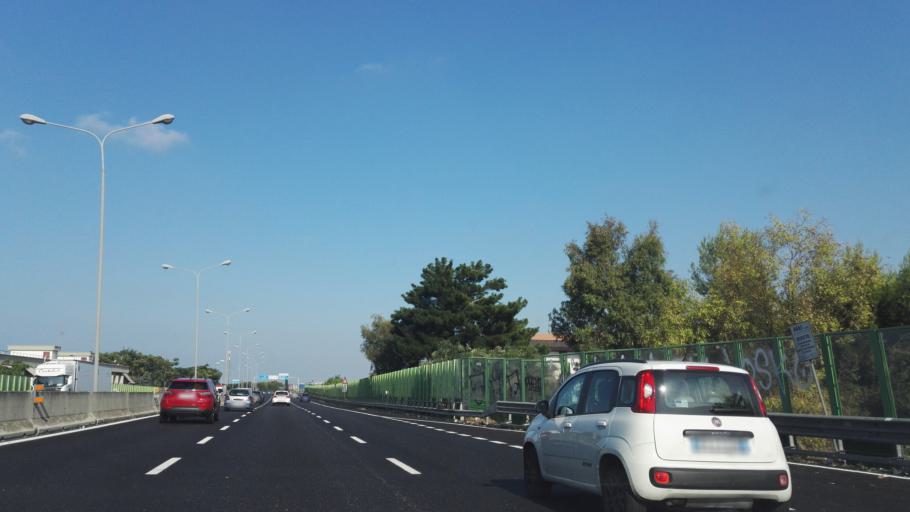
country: IT
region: Apulia
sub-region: Provincia di Bari
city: Bari
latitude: 41.0892
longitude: 16.8844
